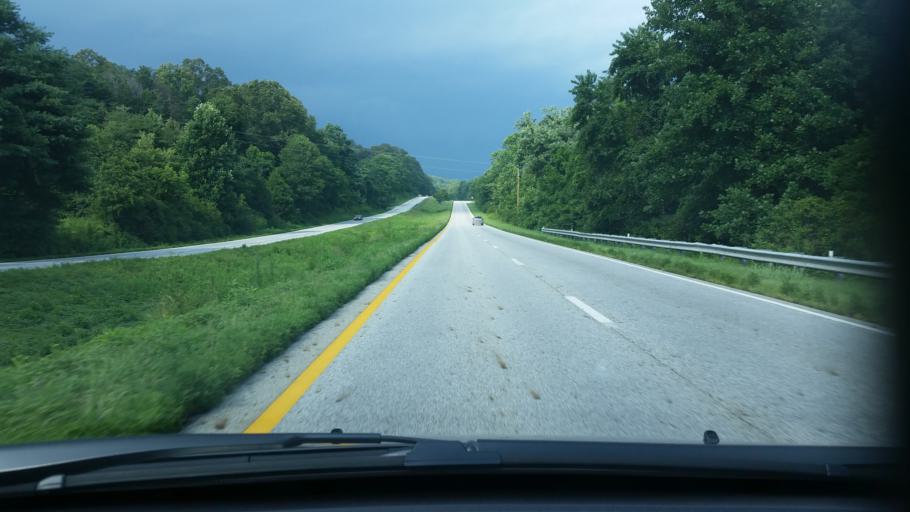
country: US
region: Virginia
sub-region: Nelson County
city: Lovingston
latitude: 37.8144
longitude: -78.8514
